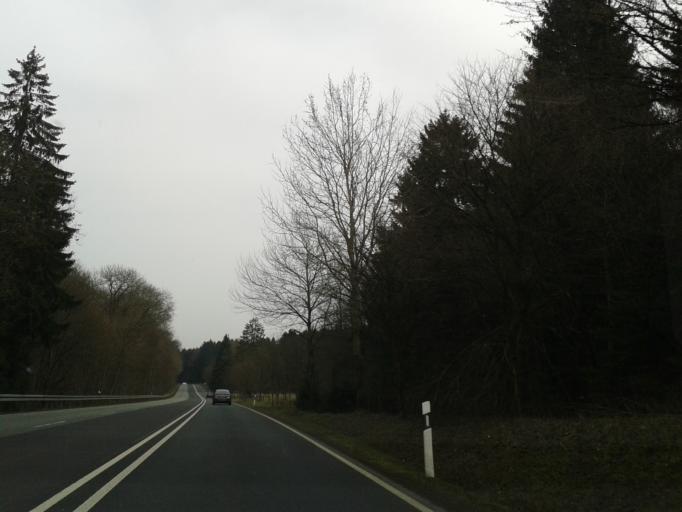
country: DE
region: Rheinland-Pfalz
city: Rehe
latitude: 50.6488
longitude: 8.1460
